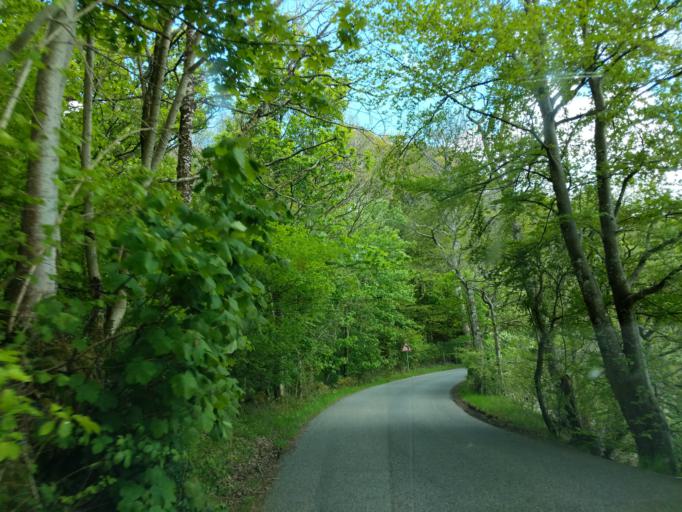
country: GB
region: Scotland
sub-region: Stirling
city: Callander
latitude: 56.1749
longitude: -4.2755
